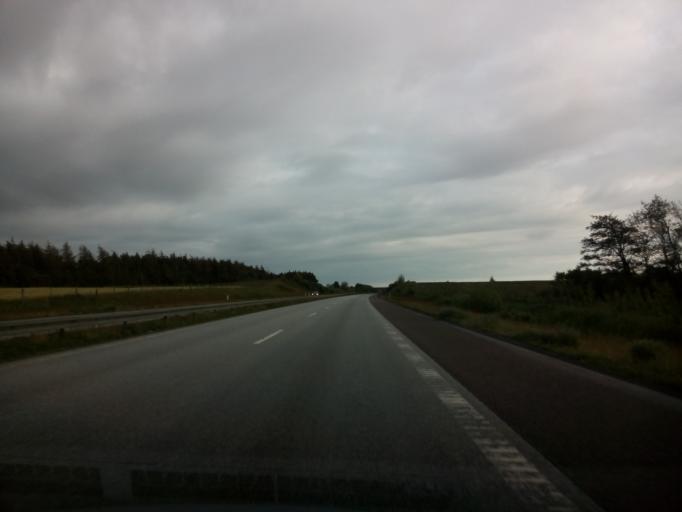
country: DK
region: North Denmark
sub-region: Hjorring Kommune
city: Hjorring
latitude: 57.4004
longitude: 10.0293
